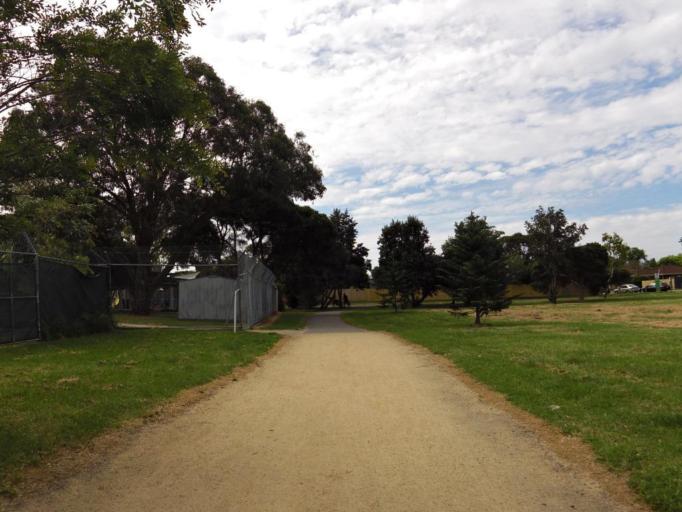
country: AU
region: Victoria
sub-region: Kingston
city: Carrum
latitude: -38.0766
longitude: 145.1311
